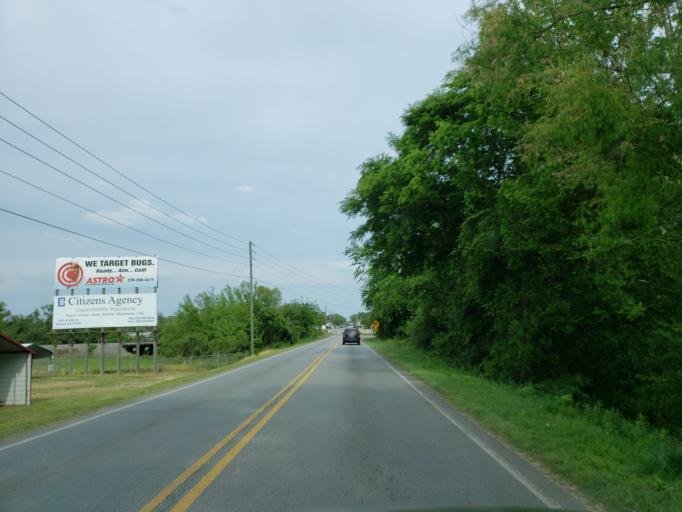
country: US
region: Georgia
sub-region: Dooly County
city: Vienna
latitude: 32.0921
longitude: -83.8016
